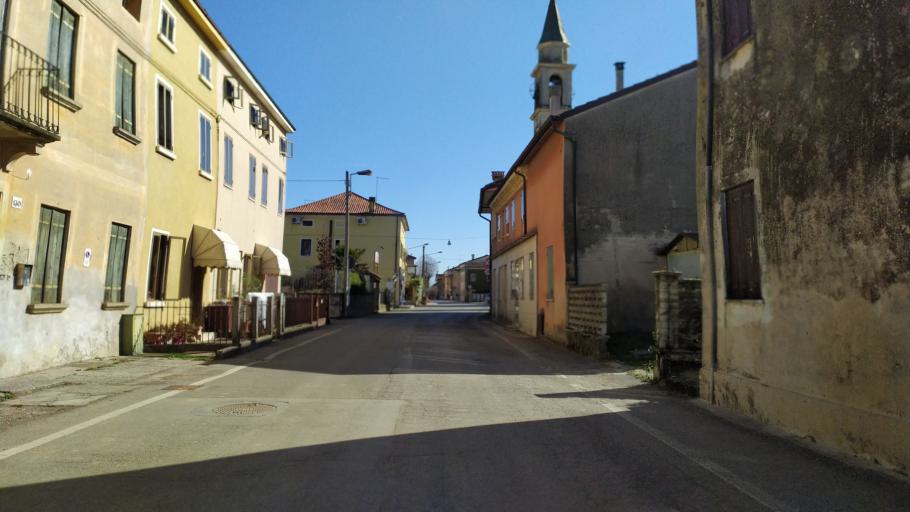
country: IT
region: Veneto
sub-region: Provincia di Vicenza
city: Monticello Conte Otto
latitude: 45.5911
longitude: 11.5498
